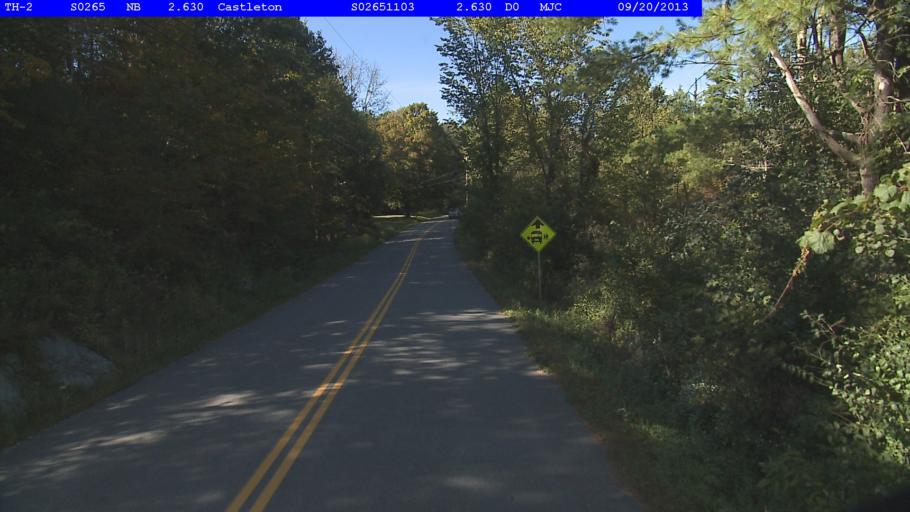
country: US
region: Vermont
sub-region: Rutland County
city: Fair Haven
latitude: 43.6390
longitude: -73.2332
